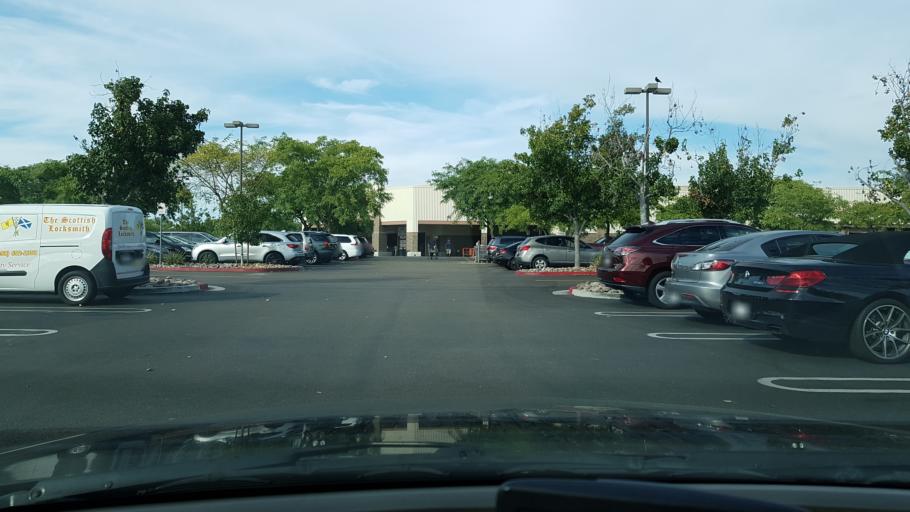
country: US
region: California
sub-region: San Diego County
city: Poway
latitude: 32.9356
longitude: -117.0333
